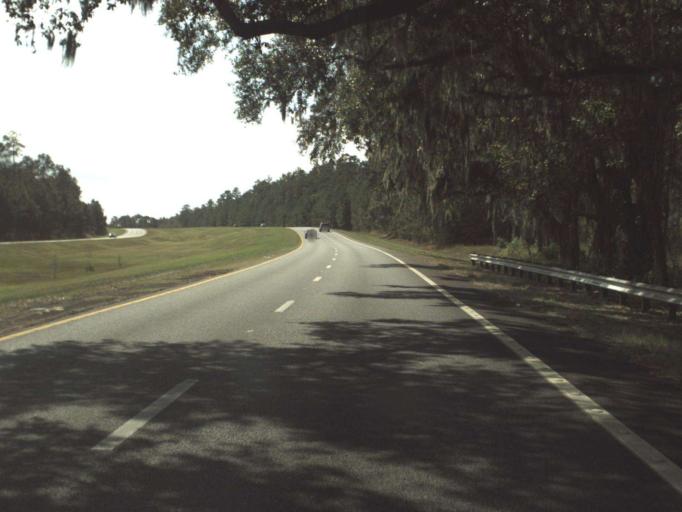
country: US
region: Georgia
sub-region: Grady County
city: Cairo
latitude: 30.6602
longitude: -84.1689
